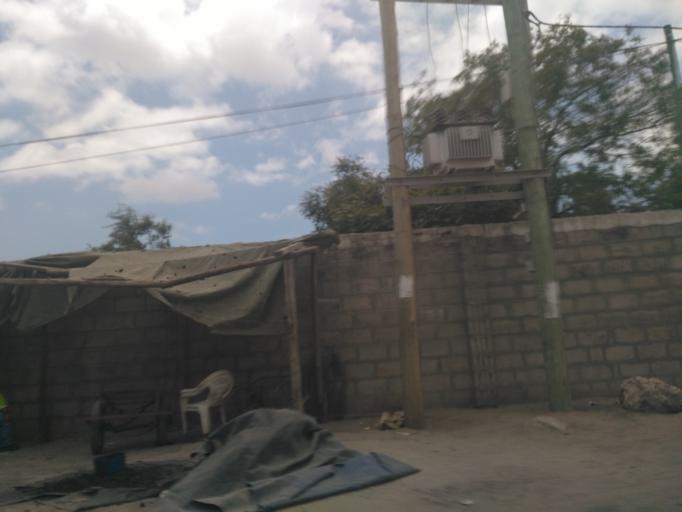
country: TZ
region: Dar es Salaam
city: Dar es Salaam
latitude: -6.8623
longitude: 39.2791
